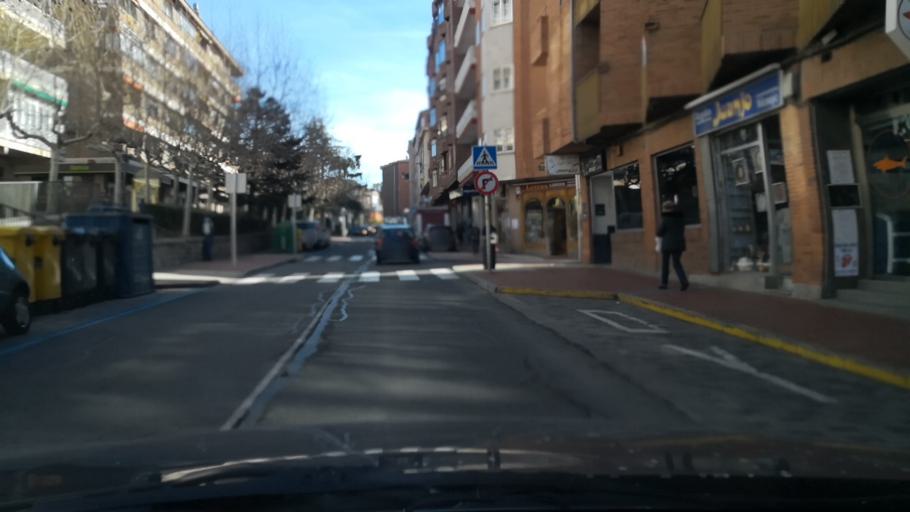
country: ES
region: Castille and Leon
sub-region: Provincia de Avila
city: Avila
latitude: 40.6537
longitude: -4.6894
